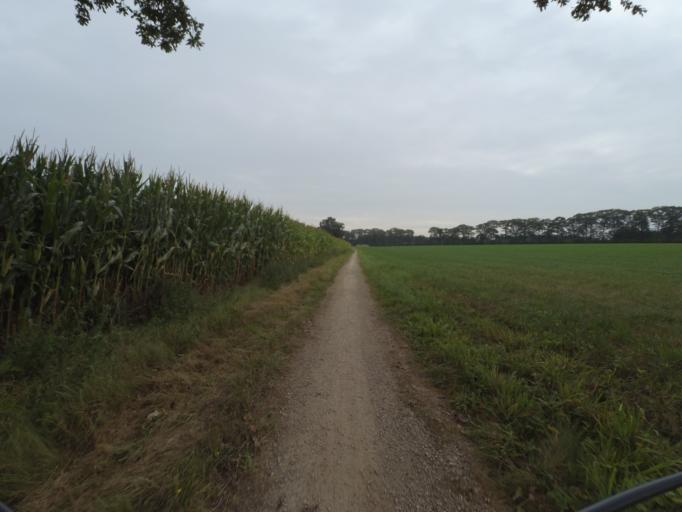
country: NL
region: Overijssel
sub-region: Gemeente Losser
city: Losser
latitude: 52.2977
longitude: 7.0137
